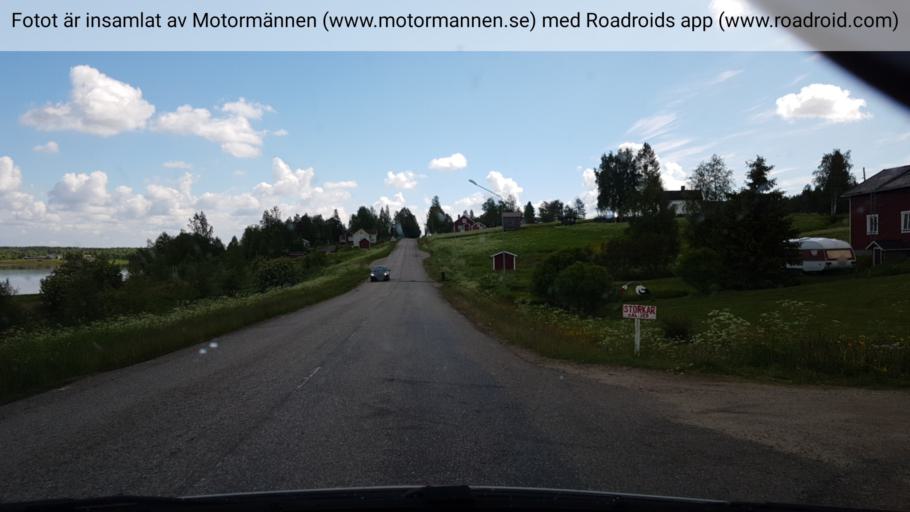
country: FI
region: Lapland
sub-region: Torniolaakso
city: Ylitornio
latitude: 66.1834
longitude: 23.7746
